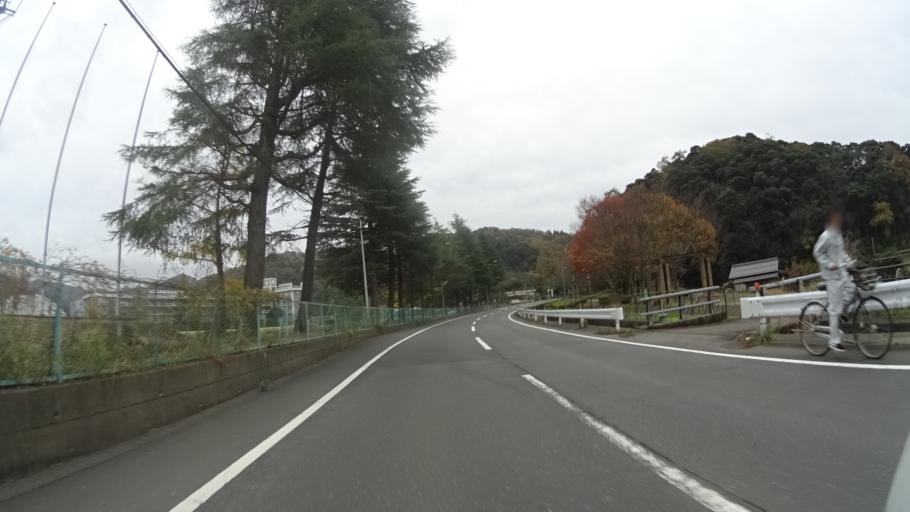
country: JP
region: Kyoto
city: Maizuru
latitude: 35.4968
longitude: 135.4374
